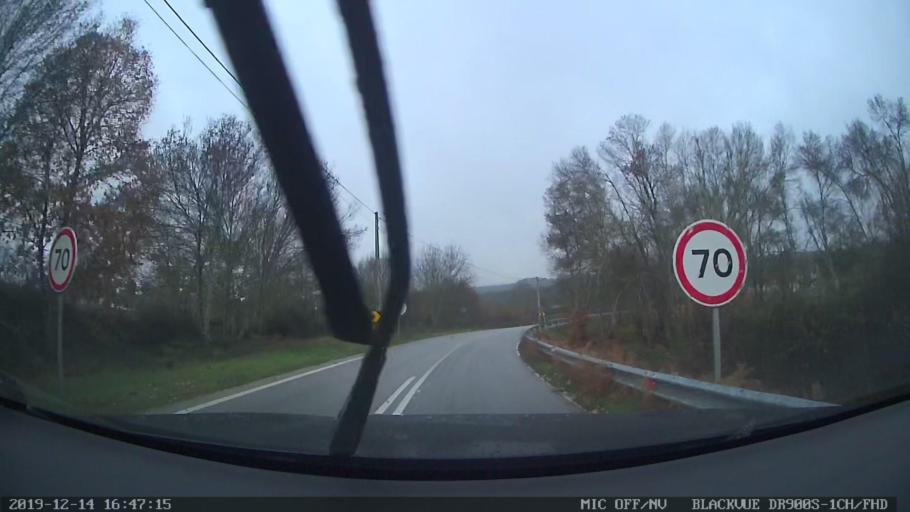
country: PT
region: Vila Real
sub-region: Murca
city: Murca
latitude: 41.3993
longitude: -7.4967
